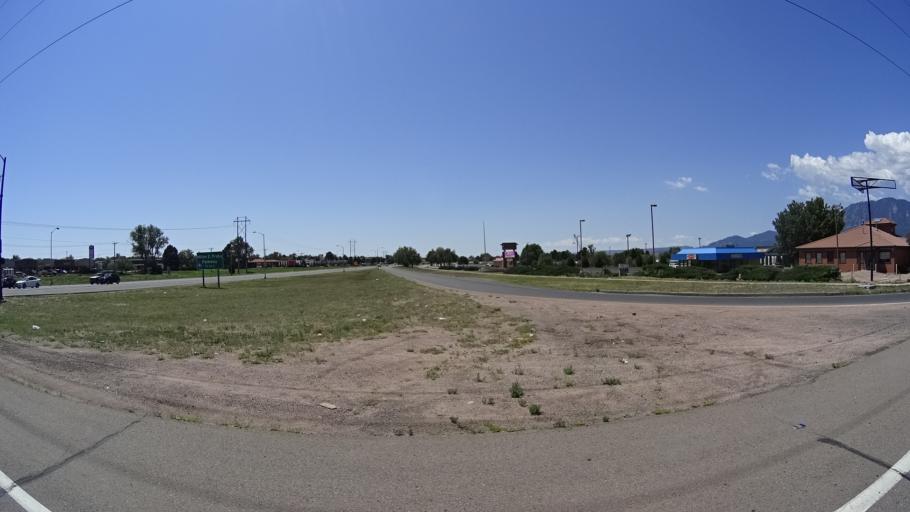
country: US
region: Colorado
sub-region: El Paso County
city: Stratmoor
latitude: 38.7890
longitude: -104.7584
